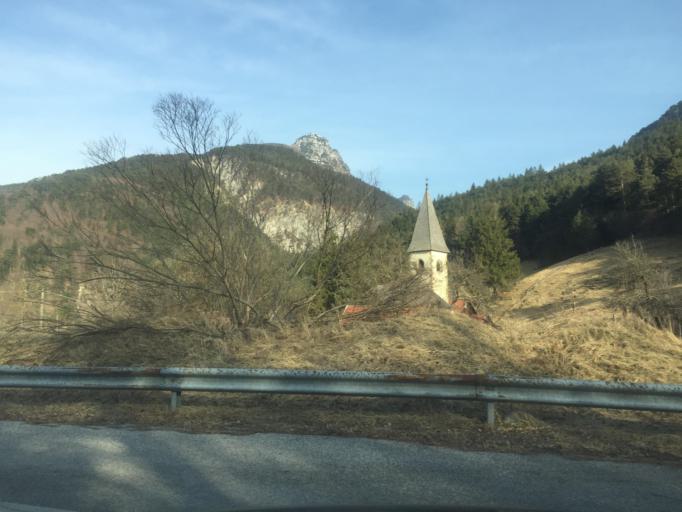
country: IT
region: Friuli Venezia Giulia
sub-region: Provincia di Udine
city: Malborghetto
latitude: 46.5021
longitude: 13.4015
